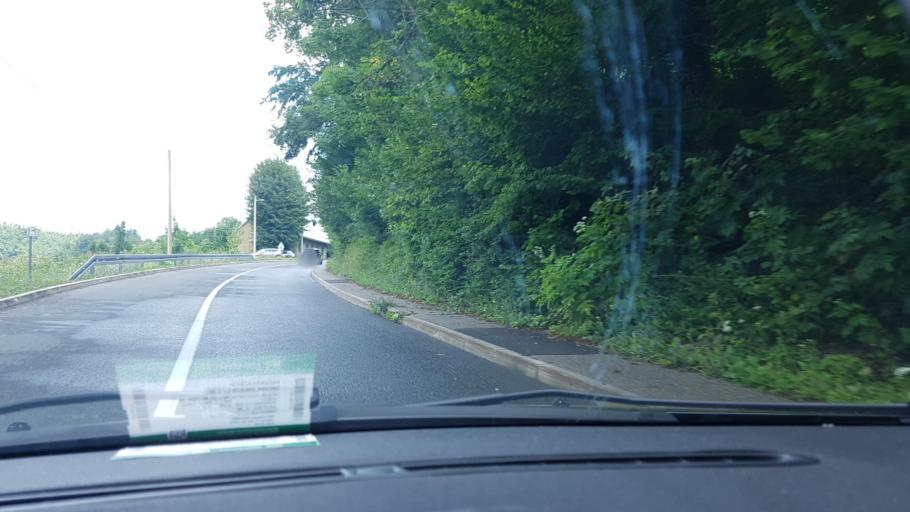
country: HR
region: Primorsko-Goranska
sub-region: Grad Delnice
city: Delnice
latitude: 45.3576
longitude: 14.7327
